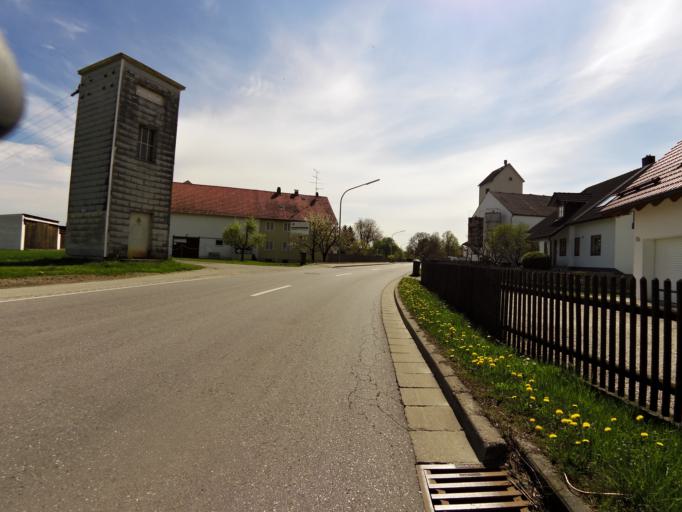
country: DE
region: Bavaria
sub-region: Lower Bavaria
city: Bruckberg
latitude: 48.5133
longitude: 12.0027
